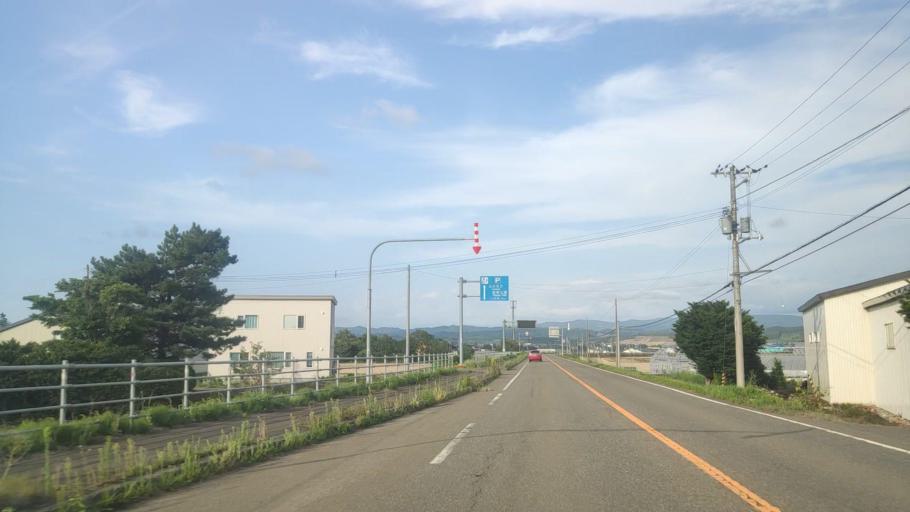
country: JP
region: Hokkaido
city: Iwamizawa
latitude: 43.0264
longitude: 141.8110
